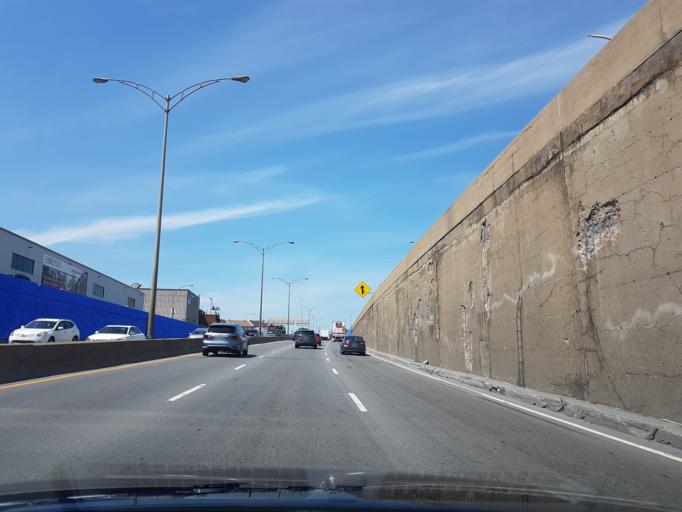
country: CA
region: Quebec
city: Montreal-Ouest
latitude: 45.4448
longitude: -73.6646
